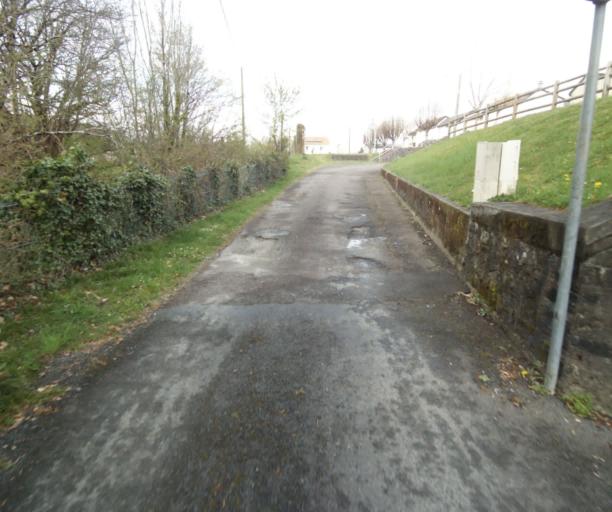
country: FR
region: Limousin
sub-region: Departement de la Correze
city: Tulle
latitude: 45.2565
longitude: 1.7385
